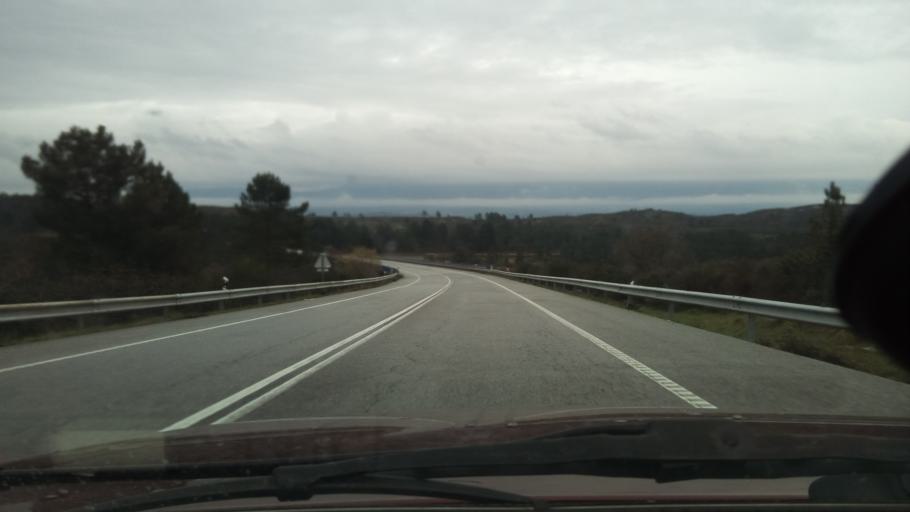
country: PT
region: Guarda
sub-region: Fornos de Algodres
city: Fornos de Algodres
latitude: 40.6036
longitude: -7.5825
